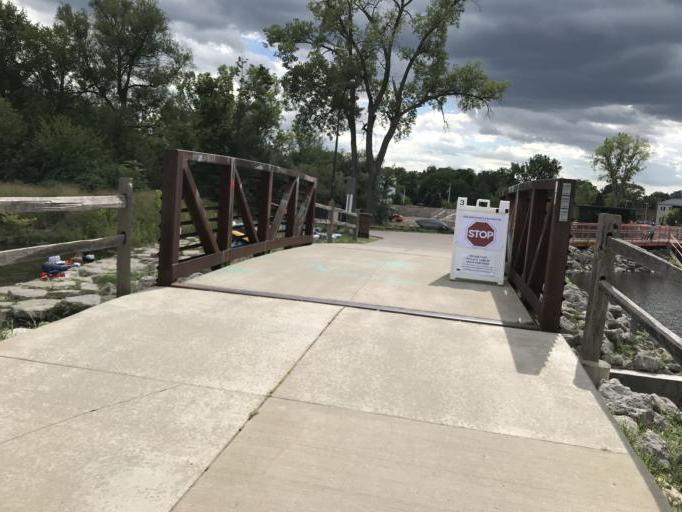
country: US
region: Michigan
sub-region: Washtenaw County
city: Ann Arbor
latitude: 42.2908
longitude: -83.7449
